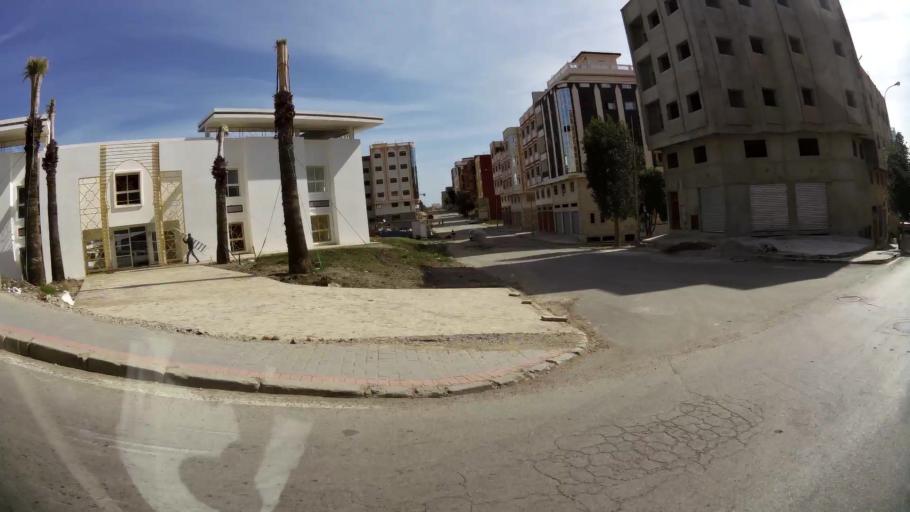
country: MA
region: Tanger-Tetouan
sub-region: Tanger-Assilah
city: Tangier
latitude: 35.7264
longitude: -5.8126
